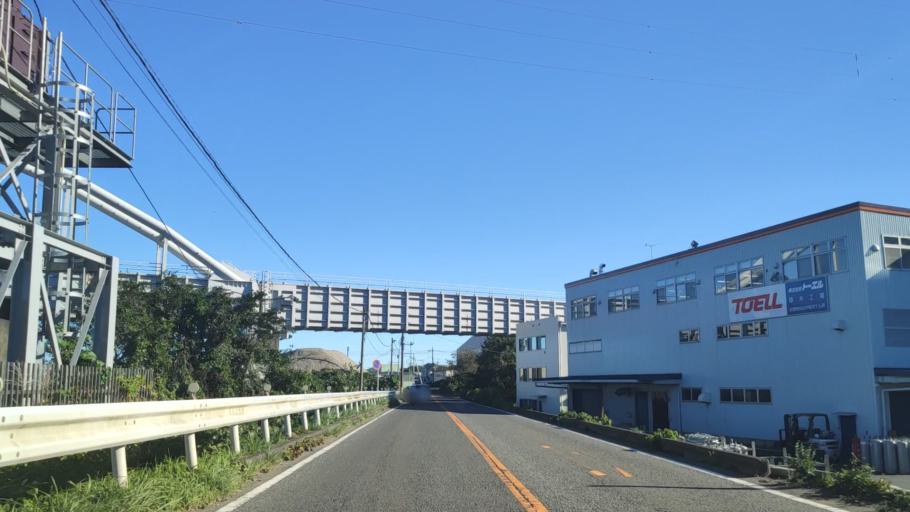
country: JP
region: Kanagawa
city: Zama
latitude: 35.5234
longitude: 139.3565
